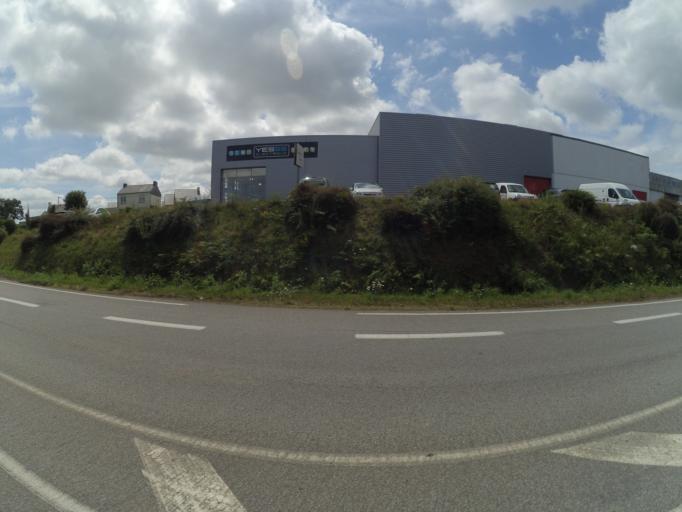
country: FR
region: Brittany
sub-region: Departement du Finistere
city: Ergue-Gaberic
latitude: 47.9874
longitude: -4.0460
